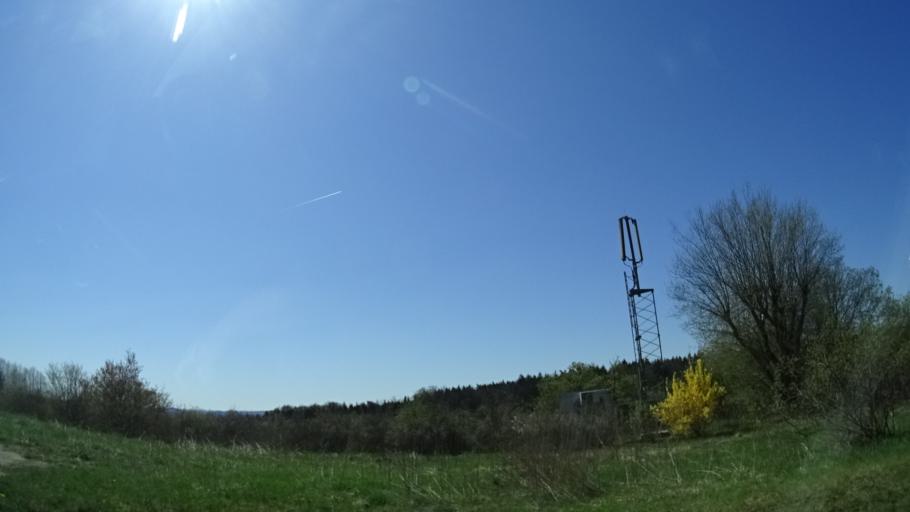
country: DE
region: Bavaria
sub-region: Regierungsbezirk Mittelfranken
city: Alfeld
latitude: 49.4101
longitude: 11.5874
